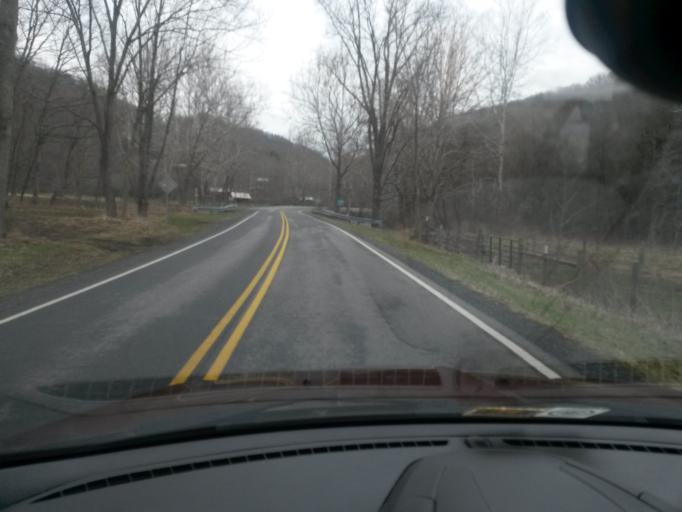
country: US
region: Virginia
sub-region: Highland County
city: Monterey
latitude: 38.3110
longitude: -79.6596
